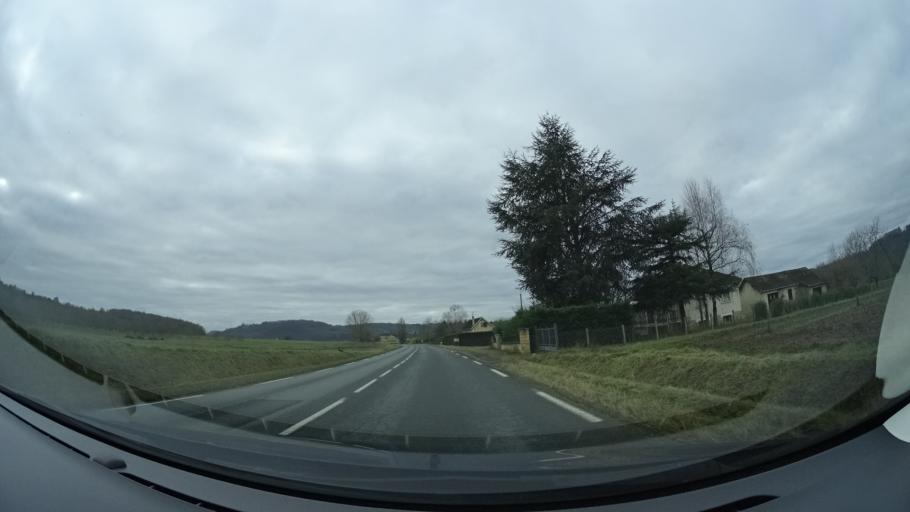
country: FR
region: Aquitaine
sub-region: Departement de la Dordogne
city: Belves
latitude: 44.8262
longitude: 1.0098
